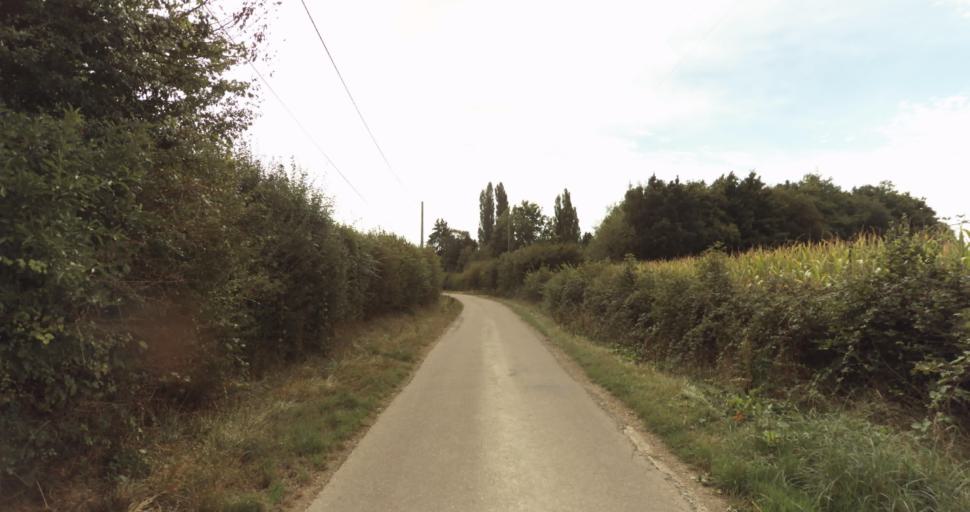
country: FR
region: Lower Normandy
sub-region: Departement du Calvados
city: La Vespiere
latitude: 48.9420
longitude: 0.3244
